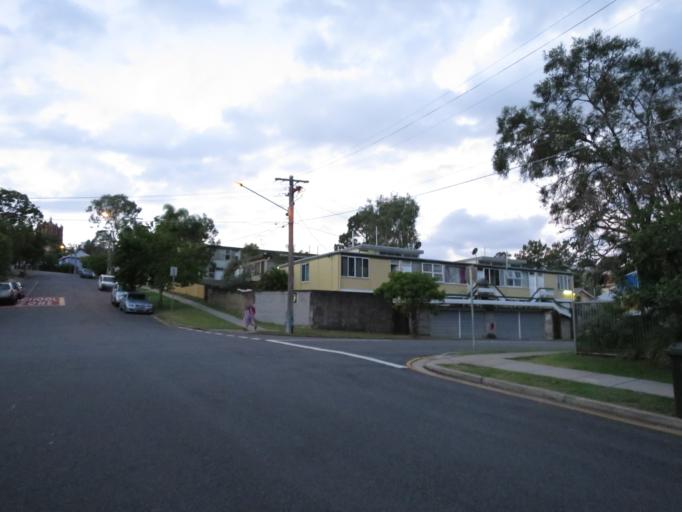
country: AU
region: Queensland
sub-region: Brisbane
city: Milton
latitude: -27.4611
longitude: 153.0101
